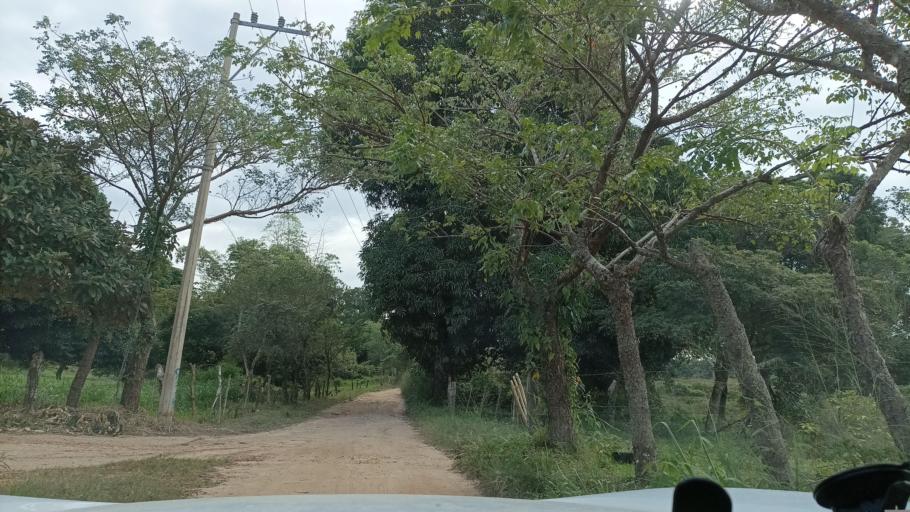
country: MX
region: Veracruz
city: Oluta
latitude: 17.9348
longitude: -94.8826
